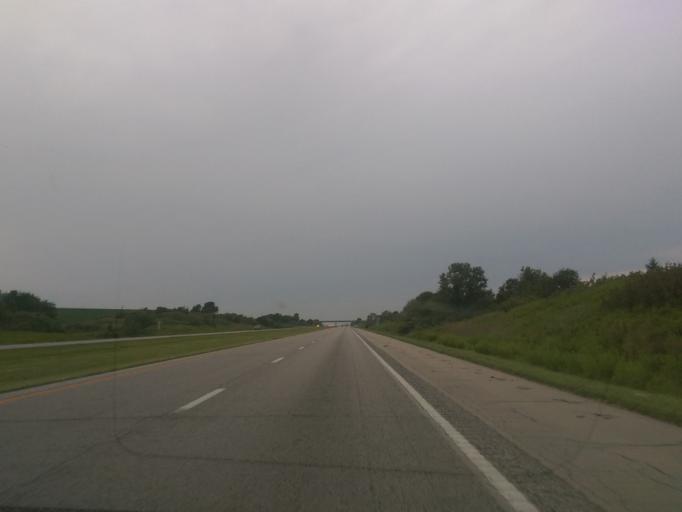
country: US
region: Missouri
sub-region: Holt County
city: Oregon
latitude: 40.0221
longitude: -95.0971
